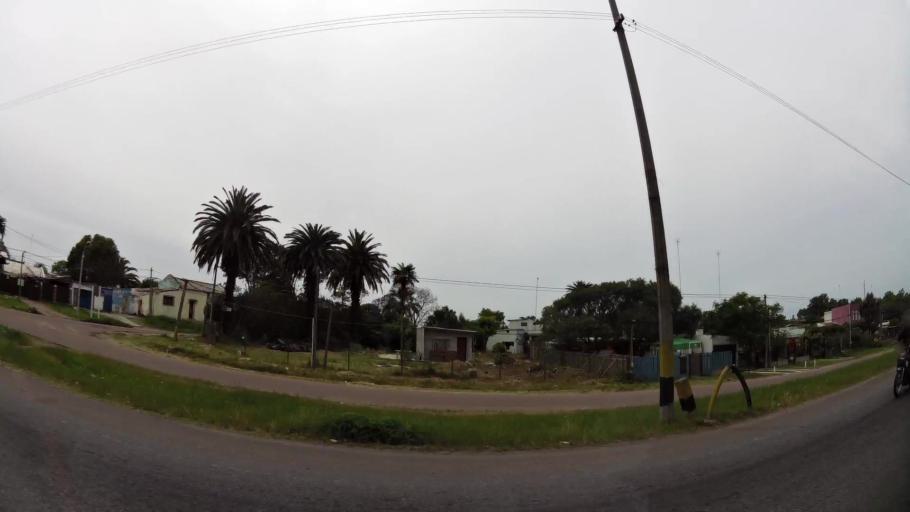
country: UY
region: Canelones
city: La Paz
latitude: -34.7922
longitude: -56.2243
